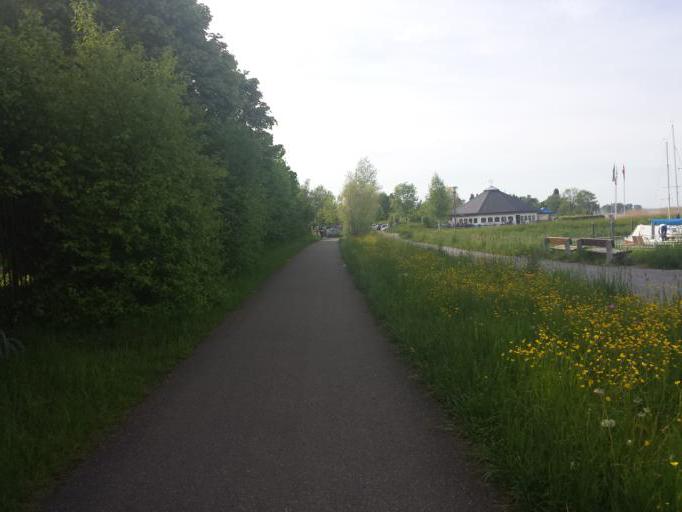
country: CH
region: Saint Gallen
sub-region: Wahlkreis Rorschach
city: Horn
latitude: 47.4992
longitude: 9.4517
